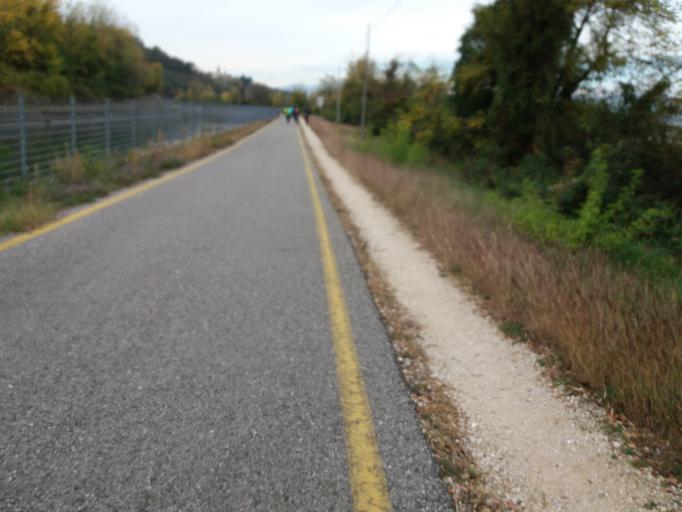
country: IT
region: Veneto
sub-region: Provincia di Verona
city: Pastrengo
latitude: 45.4997
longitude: 10.8086
